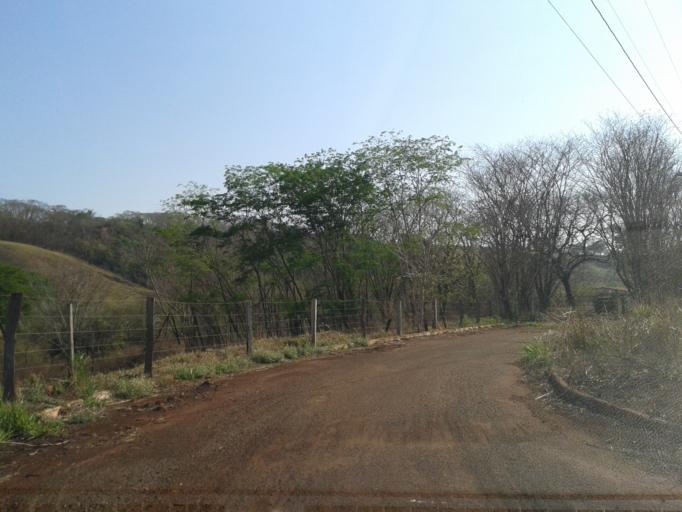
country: BR
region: Minas Gerais
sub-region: Ituiutaba
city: Ituiutaba
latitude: -18.9444
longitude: -49.4549
